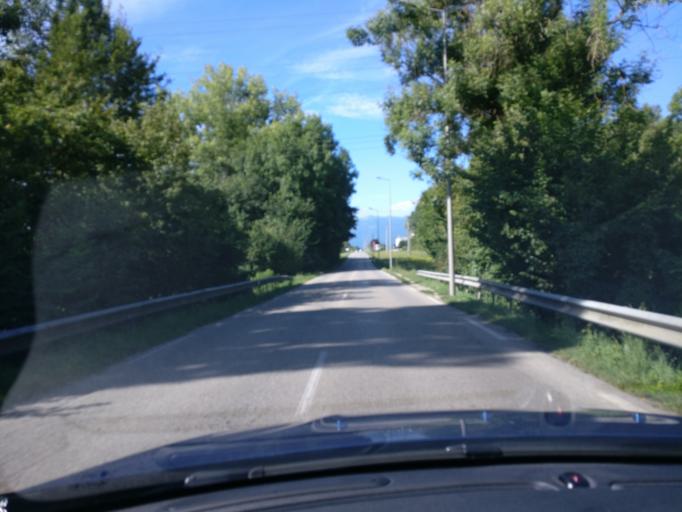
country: FR
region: Rhone-Alpes
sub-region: Departement de l'Ain
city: Saint-Genis-Pouilly
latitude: 46.2392
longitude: 6.0141
